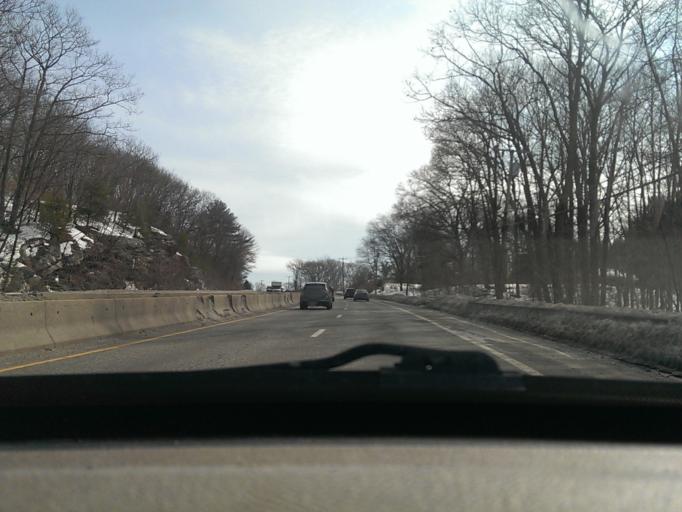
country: US
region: Massachusetts
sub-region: Worcester County
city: Millbury
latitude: 42.1816
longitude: -71.7622
